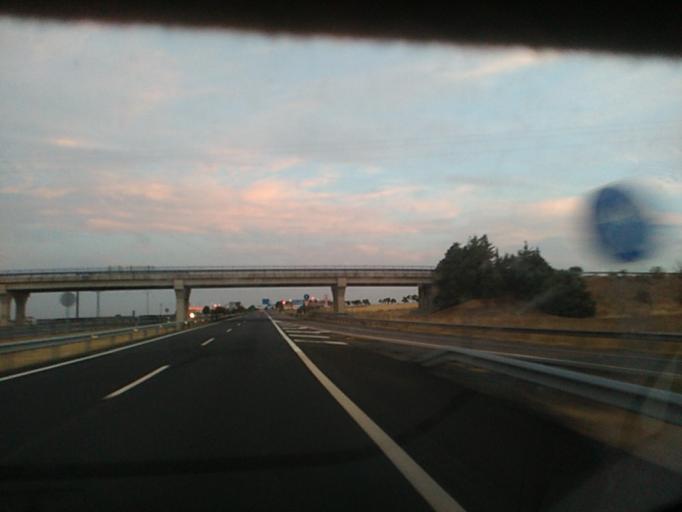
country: ES
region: Castille and Leon
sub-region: Provincia de Avila
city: Adanero
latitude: 40.9519
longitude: -4.6098
